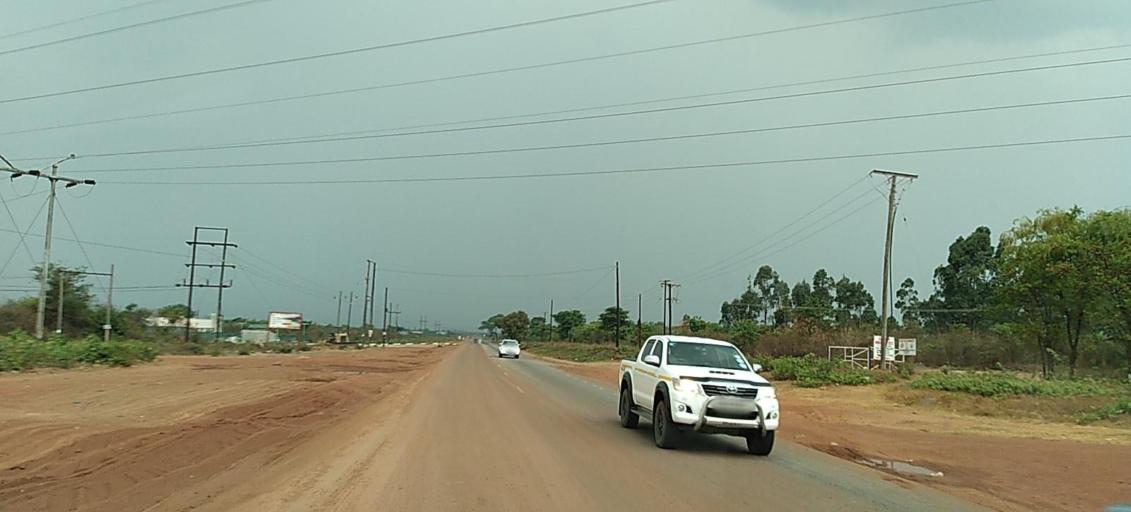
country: ZM
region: Copperbelt
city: Kalulushi
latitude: -12.8337
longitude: 28.1111
